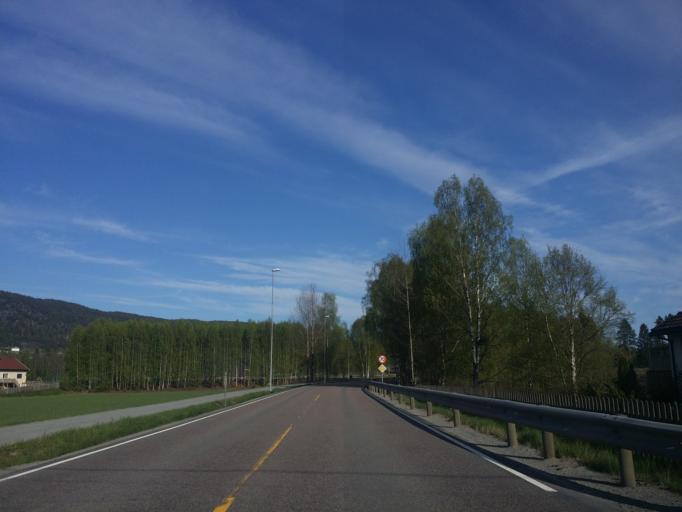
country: NO
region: Telemark
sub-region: Notodden
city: Notodden
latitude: 59.5921
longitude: 9.1488
